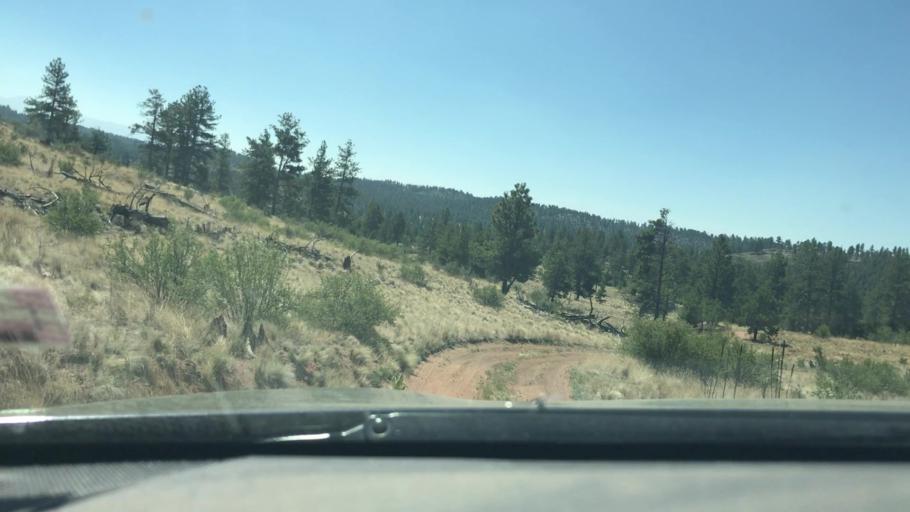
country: US
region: Colorado
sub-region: Teller County
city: Woodland Park
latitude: 39.0014
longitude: -105.3463
